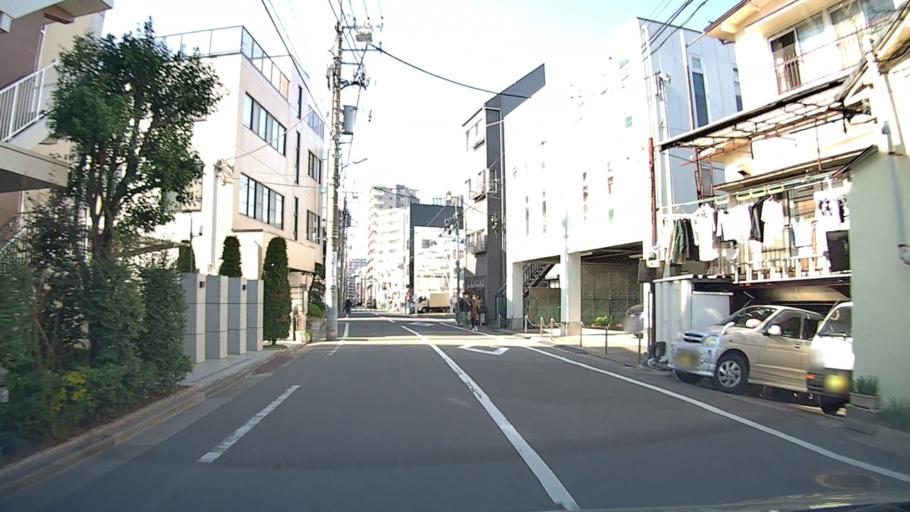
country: JP
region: Tokyo
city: Tokyo
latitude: 35.7336
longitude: 139.6576
